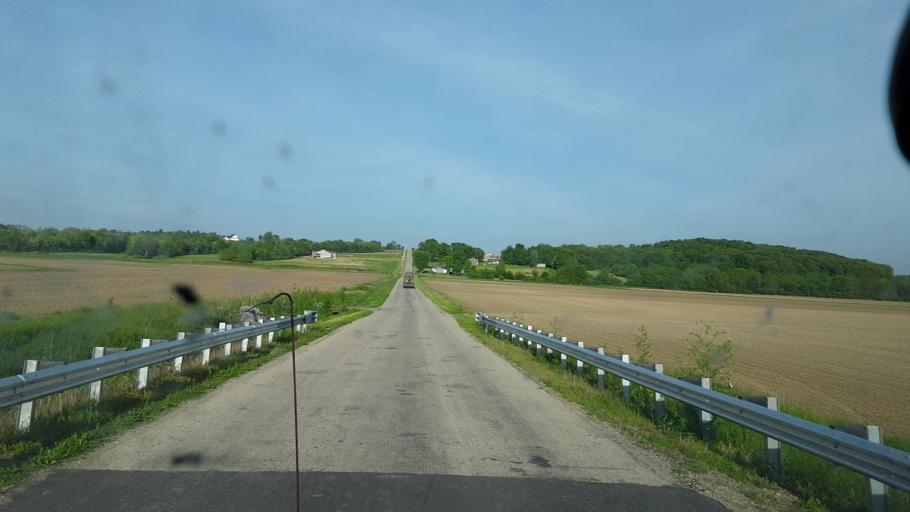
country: US
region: Ohio
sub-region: Ross County
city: Kingston
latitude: 39.5128
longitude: -82.7684
